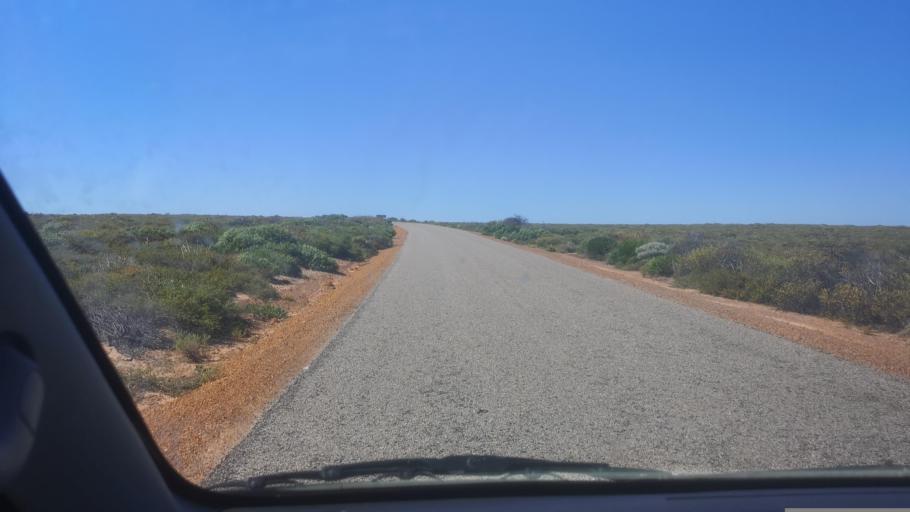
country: AU
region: Western Australia
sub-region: Northampton Shire
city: Kalbarri
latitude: -27.8266
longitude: 114.1165
